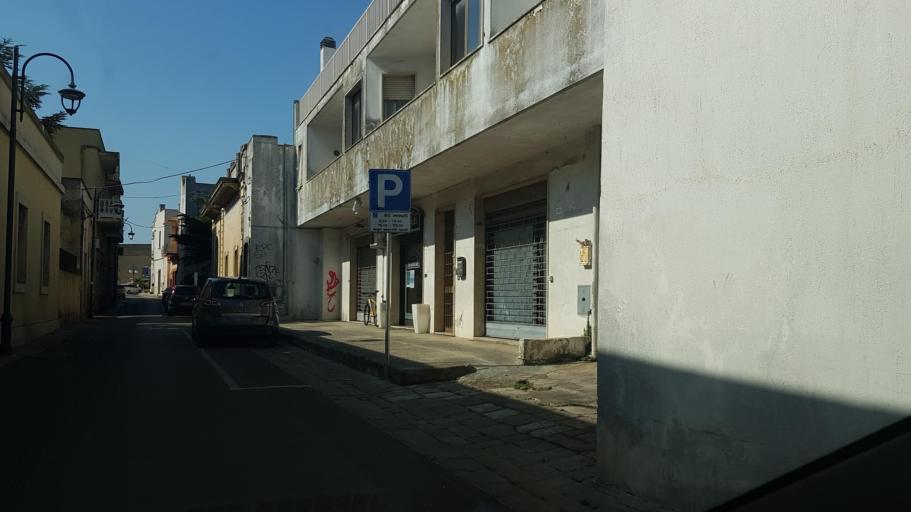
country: IT
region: Apulia
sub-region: Provincia di Lecce
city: Taurisano
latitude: 39.9567
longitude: 18.2138
